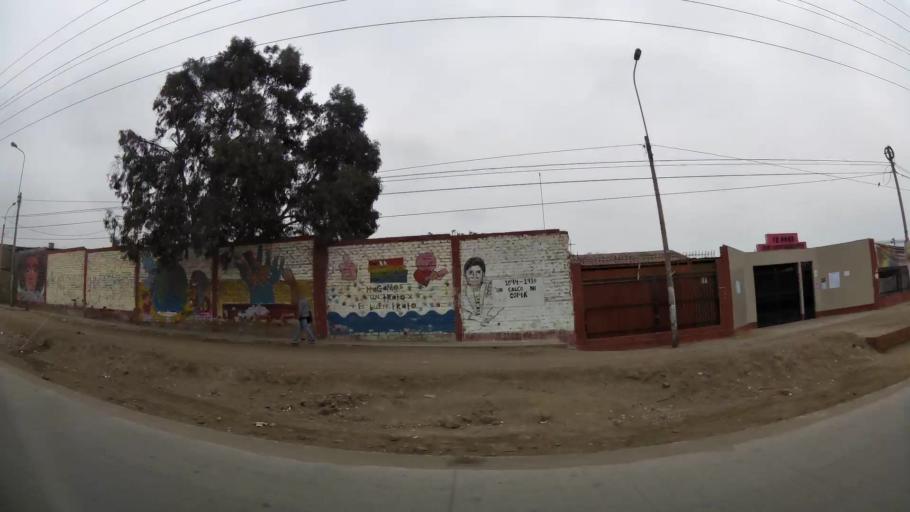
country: PE
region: Lima
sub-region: Lima
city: Surco
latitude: -12.2006
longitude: -76.9432
